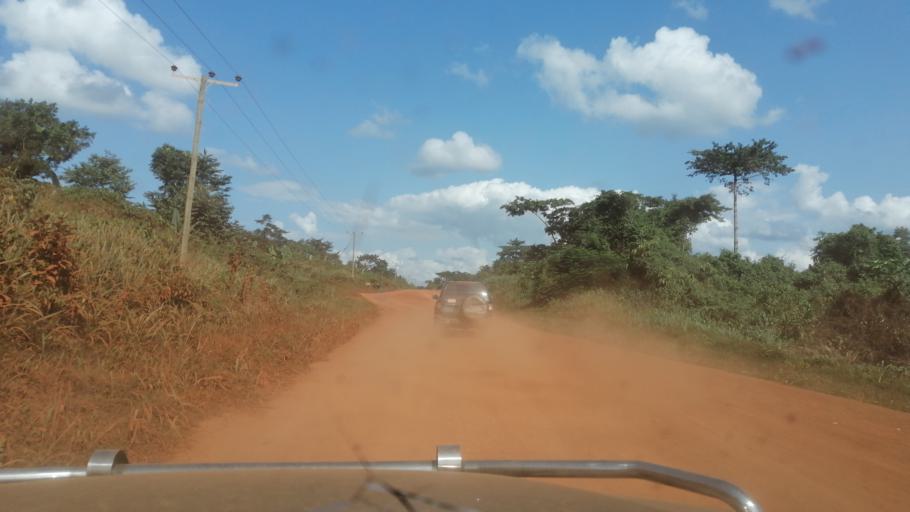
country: GH
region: Western
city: Bibiani
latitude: 6.6951
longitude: -2.5711
